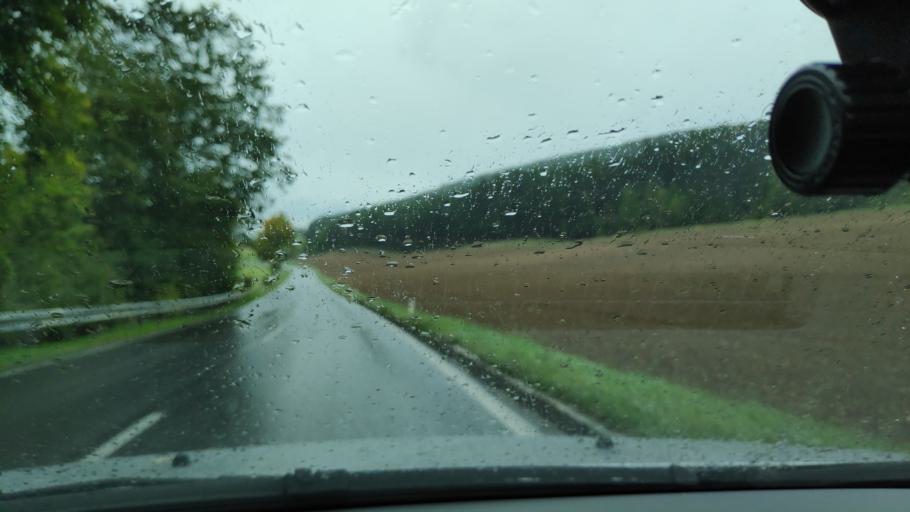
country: AT
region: Lower Austria
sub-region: Politischer Bezirk Neunkirchen
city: Schrattenbach
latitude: 47.7910
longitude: 16.0147
